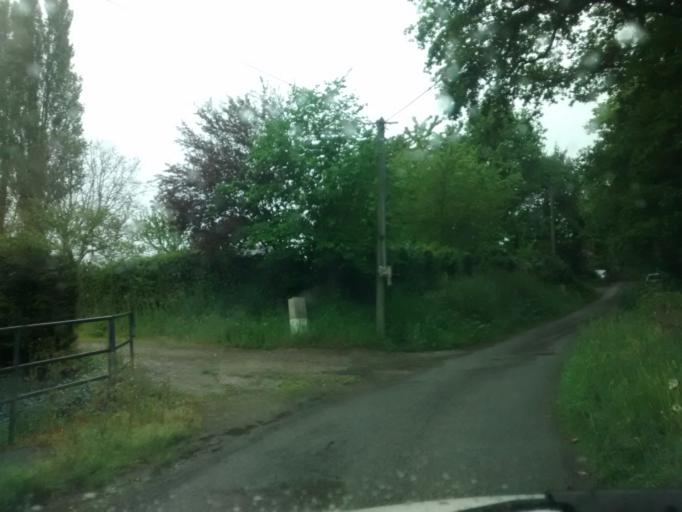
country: FR
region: Brittany
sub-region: Departement d'Ille-et-Vilaine
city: Acigne
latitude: 48.1115
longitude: -1.5670
